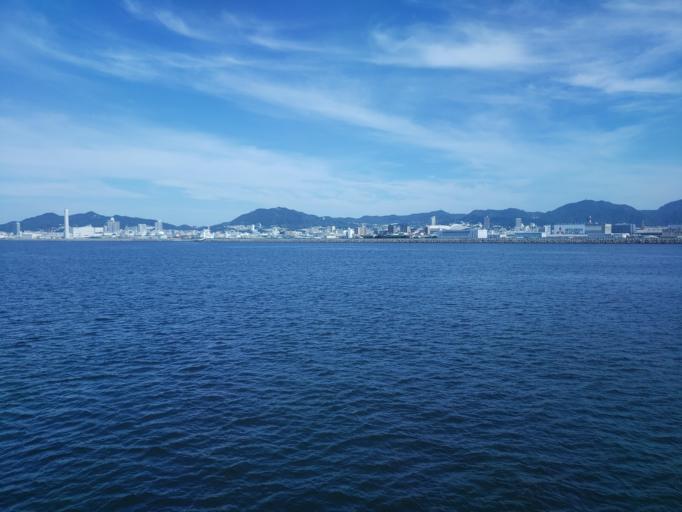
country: JP
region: Hyogo
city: Kobe
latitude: 34.6418
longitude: 135.1803
